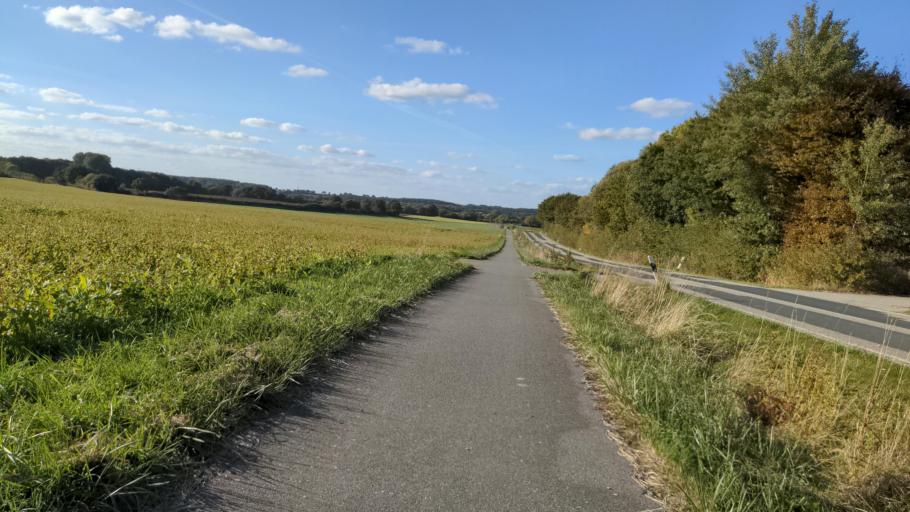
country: DE
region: Schleswig-Holstein
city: Zarpen
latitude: 53.8601
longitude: 10.5385
